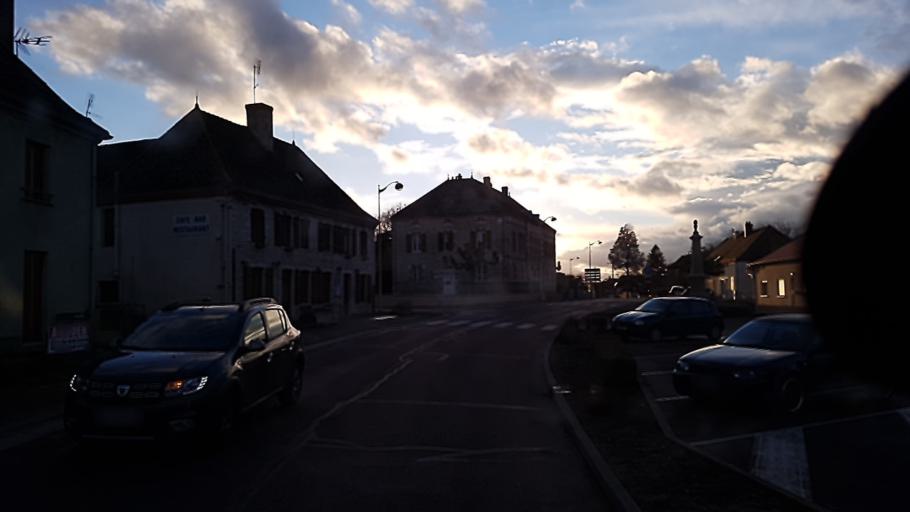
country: FR
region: Bourgogne
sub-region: Departement de Saone-et-Loire
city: Saint-Germain-du-Plain
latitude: 46.7057
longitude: 5.0520
